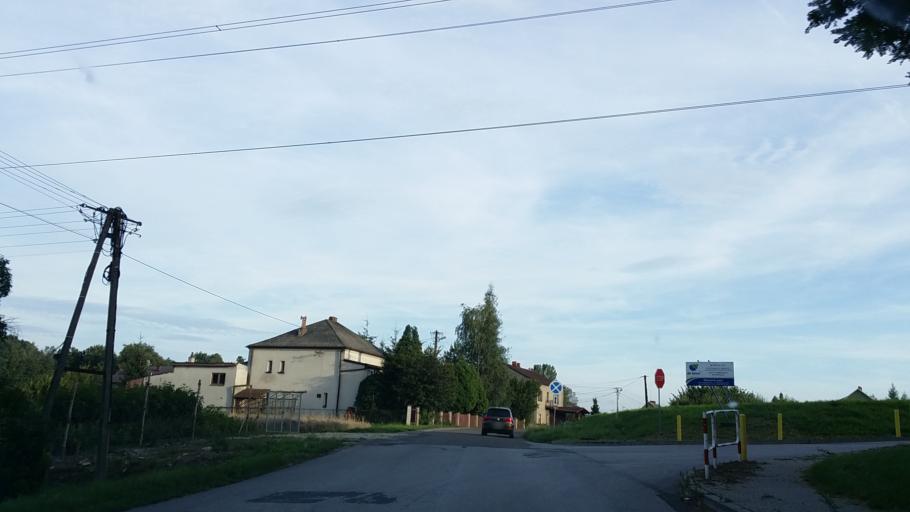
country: PL
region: Lesser Poland Voivodeship
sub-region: Powiat wadowicki
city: Spytkowice
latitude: 49.9815
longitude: 19.5023
